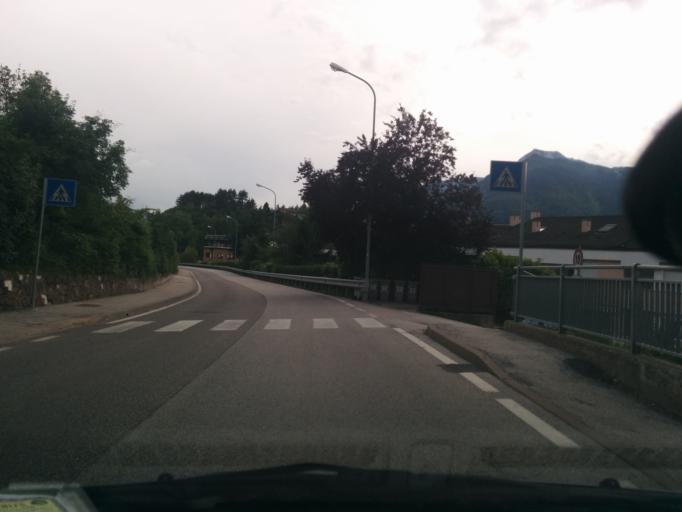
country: IT
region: Trentino-Alto Adige
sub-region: Provincia di Trento
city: Trento
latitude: 46.0886
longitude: 11.1329
